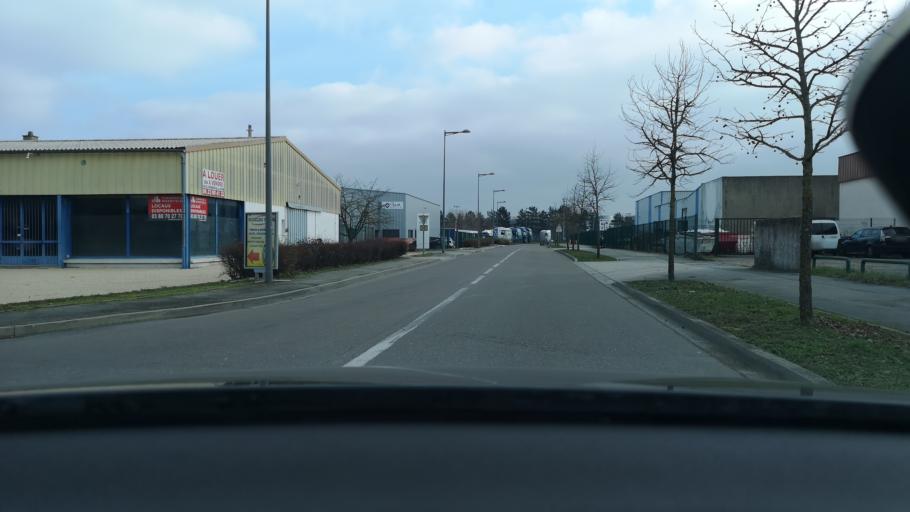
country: FR
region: Bourgogne
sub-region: Departement de Saone-et-Loire
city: Chatenoy-le-Royal
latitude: 46.7980
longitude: 4.8287
